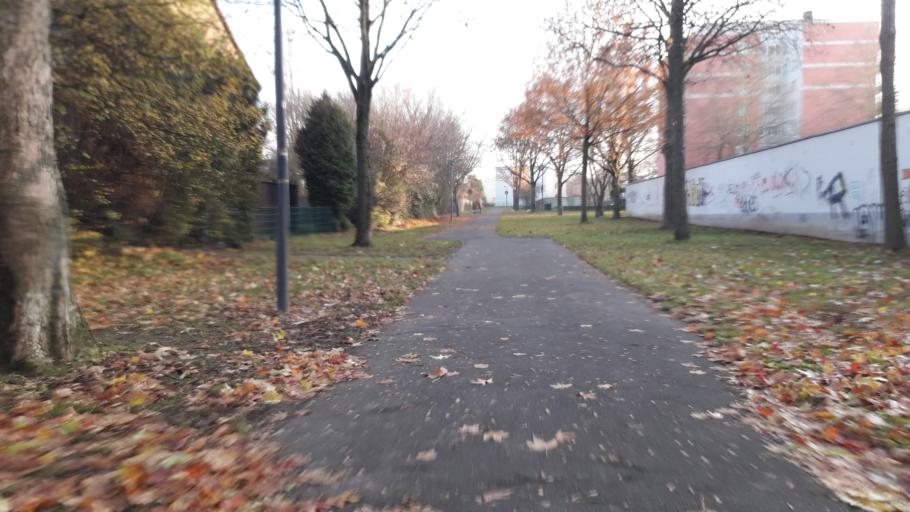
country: DE
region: North Rhine-Westphalia
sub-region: Regierungsbezirk Detmold
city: Paderborn
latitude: 51.7273
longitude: 8.7805
